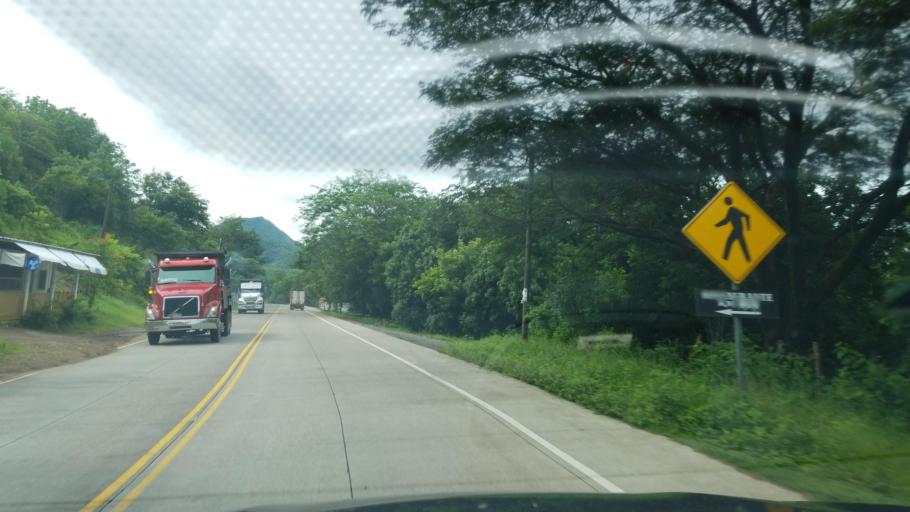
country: HN
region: Choluteca
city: Pespire
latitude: 13.6220
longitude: -87.3741
